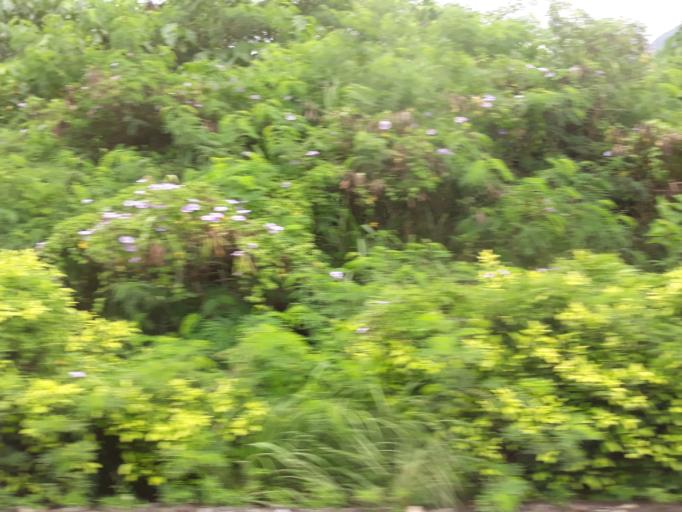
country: TW
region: Taiwan
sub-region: Yilan
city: Yilan
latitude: 24.4377
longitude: 121.7810
